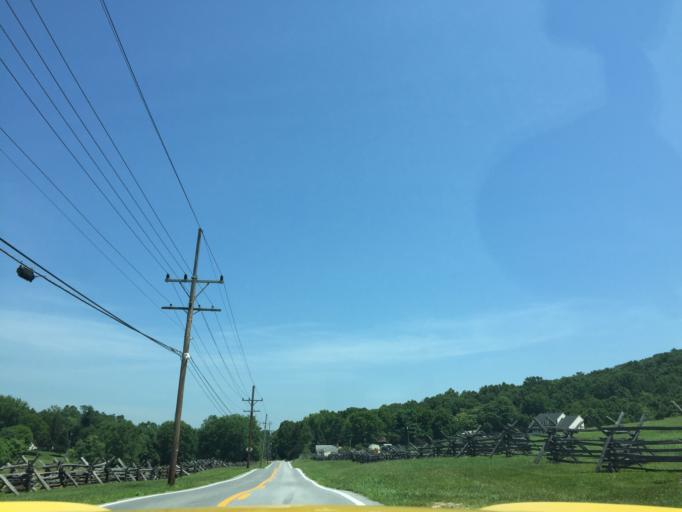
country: US
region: West Virginia
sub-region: Jefferson County
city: Bolivar
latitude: 39.3252
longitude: -77.7666
